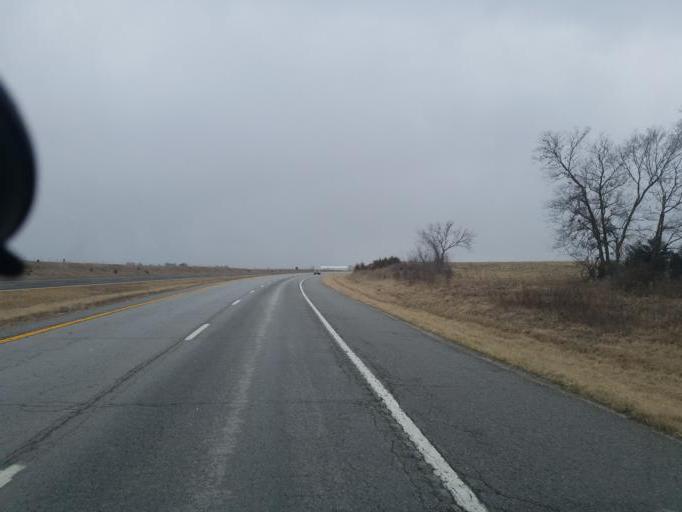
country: US
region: Missouri
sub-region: Macon County
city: La Plata
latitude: 39.8902
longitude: -92.4711
